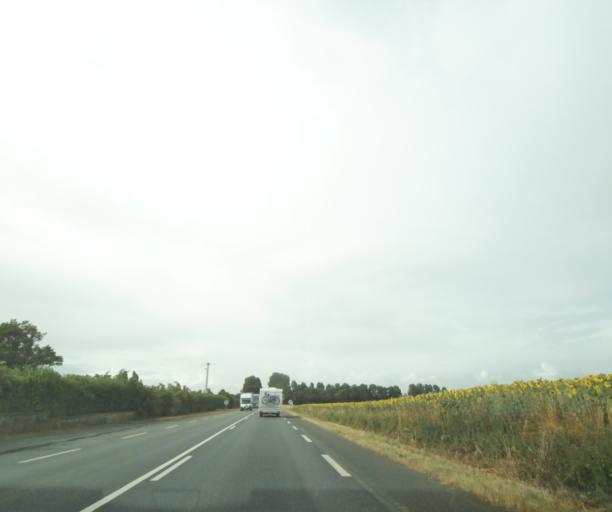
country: FR
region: Pays de la Loire
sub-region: Departement de la Vendee
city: Sainte-Gemme-la-Plaine
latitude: 46.4499
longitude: -1.1036
